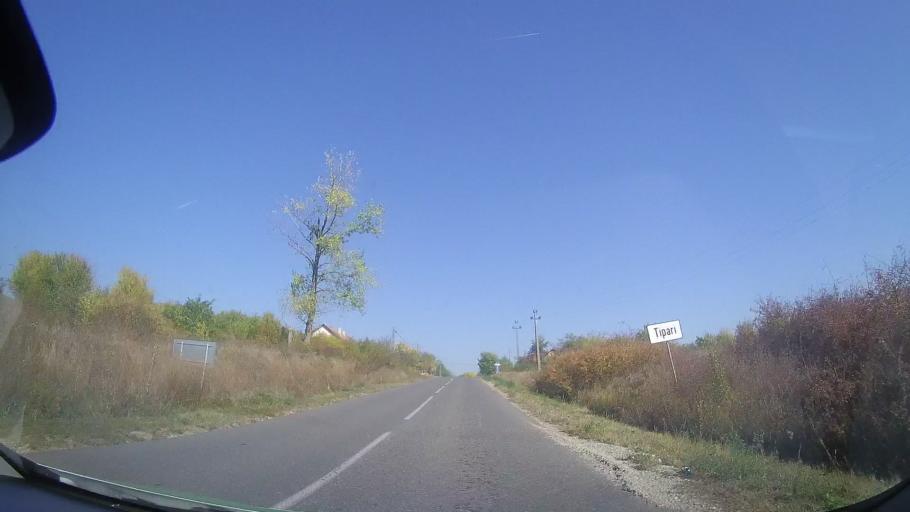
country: RO
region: Timis
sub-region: Comuna Costeiu
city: Costeiu
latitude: 45.7577
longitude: 21.8484
